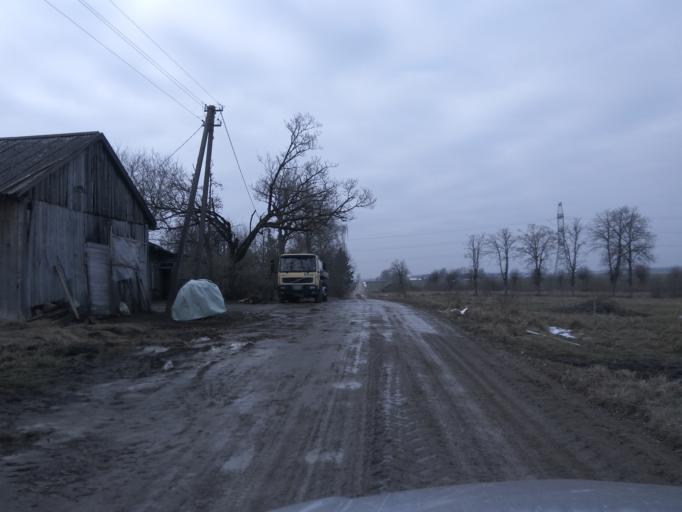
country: LV
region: Durbe
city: Liegi
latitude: 56.6719
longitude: 21.3561
